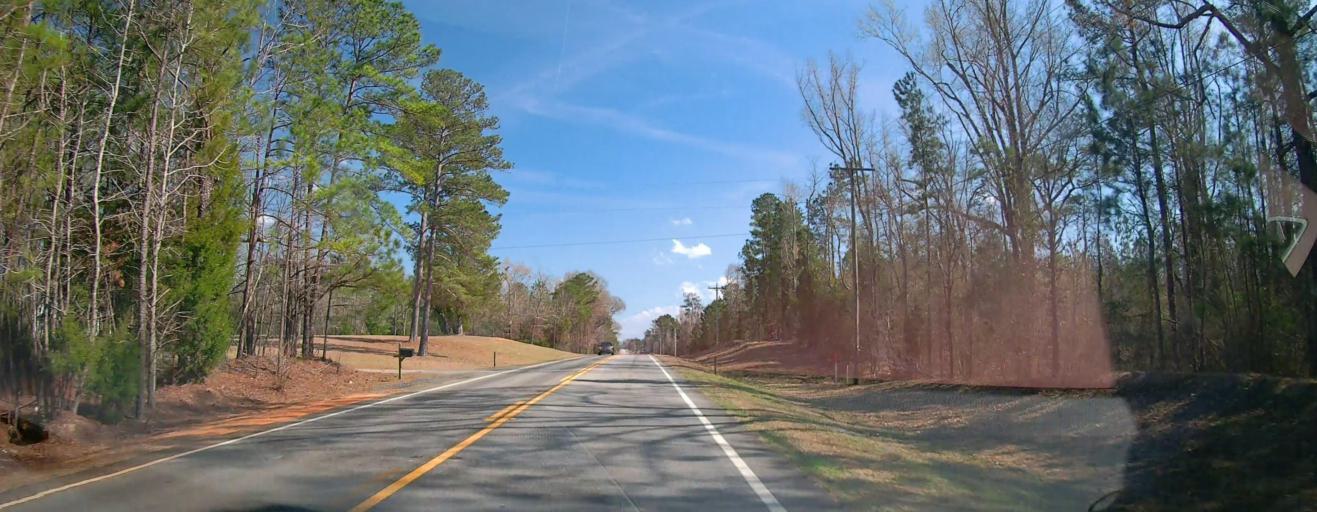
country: US
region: Georgia
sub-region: Wilkinson County
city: Gordon
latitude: 32.8979
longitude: -83.3659
